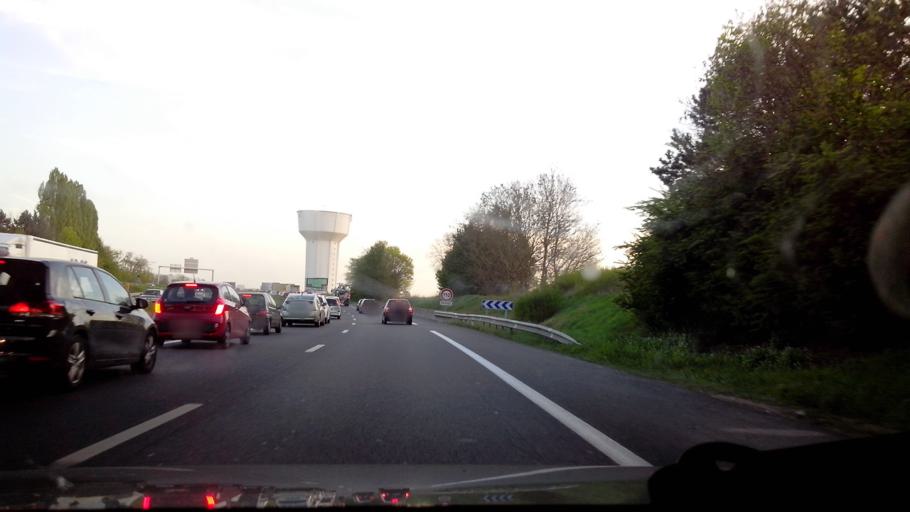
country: FR
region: Ile-de-France
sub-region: Departement de l'Essonne
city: Saclay
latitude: 48.7293
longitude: 2.1656
